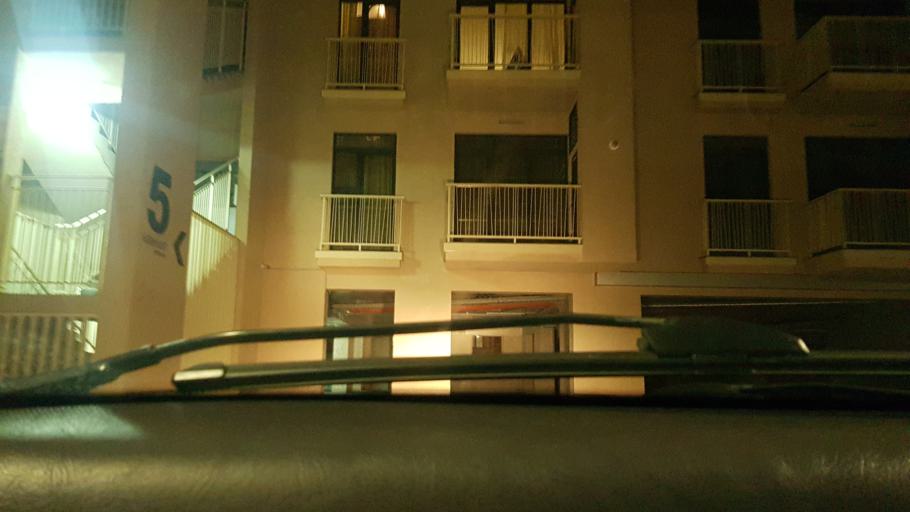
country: GE
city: Tsqnet'i
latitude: 41.7233
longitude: 44.7491
